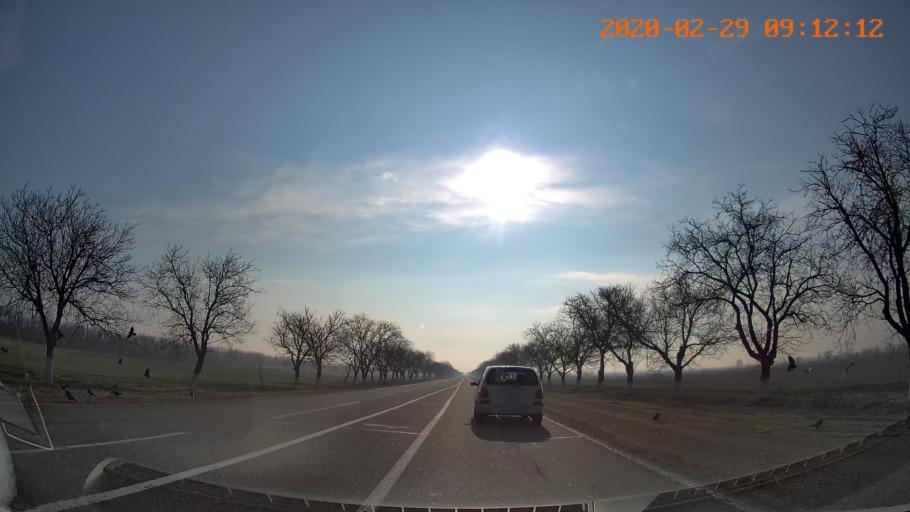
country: MD
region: Telenesti
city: Slobozia
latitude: 46.8287
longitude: 29.8127
